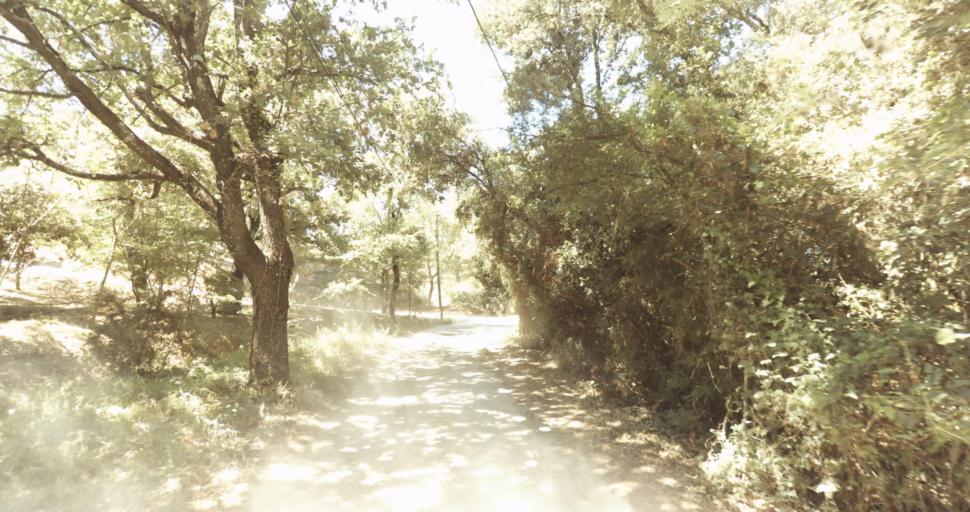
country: FR
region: Provence-Alpes-Cote d'Azur
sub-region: Departement du Var
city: Gassin
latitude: 43.2367
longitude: 6.5670
